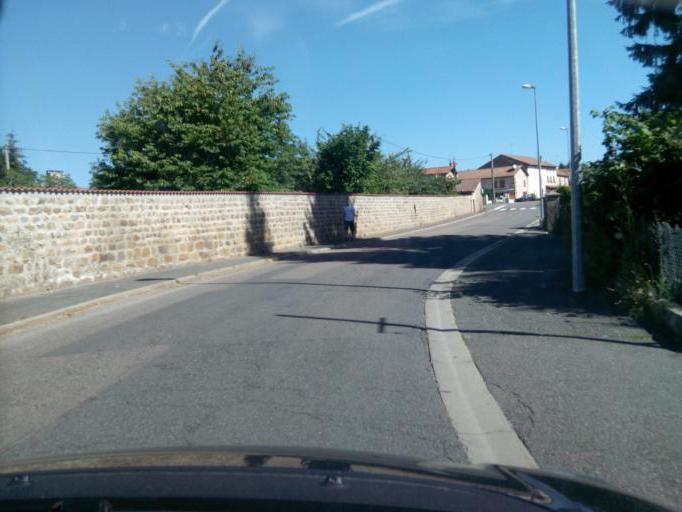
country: FR
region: Rhone-Alpes
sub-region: Departement de la Loire
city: Usson-en-Forez
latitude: 45.3803
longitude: 3.9966
